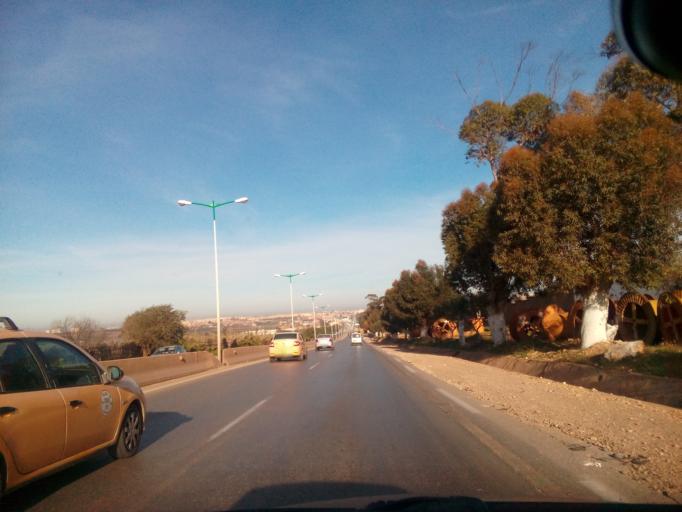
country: DZ
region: Mostaganem
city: Mostaganem
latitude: 35.8946
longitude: 0.1275
